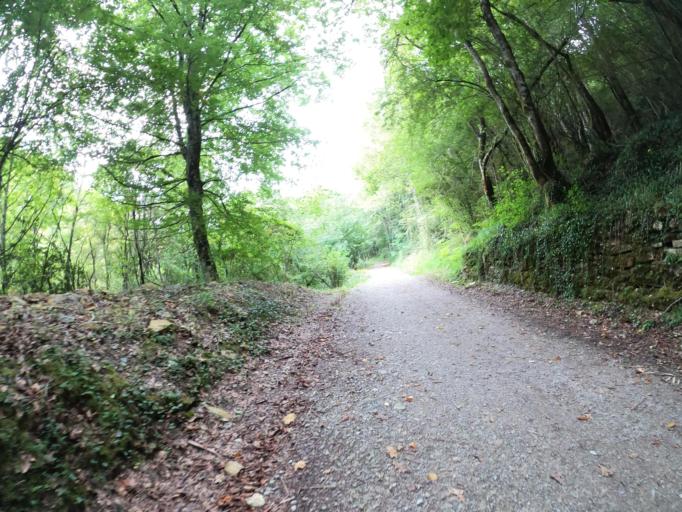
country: ES
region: Navarre
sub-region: Provincia de Navarra
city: Lekunberri
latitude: 42.9837
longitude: -1.8698
